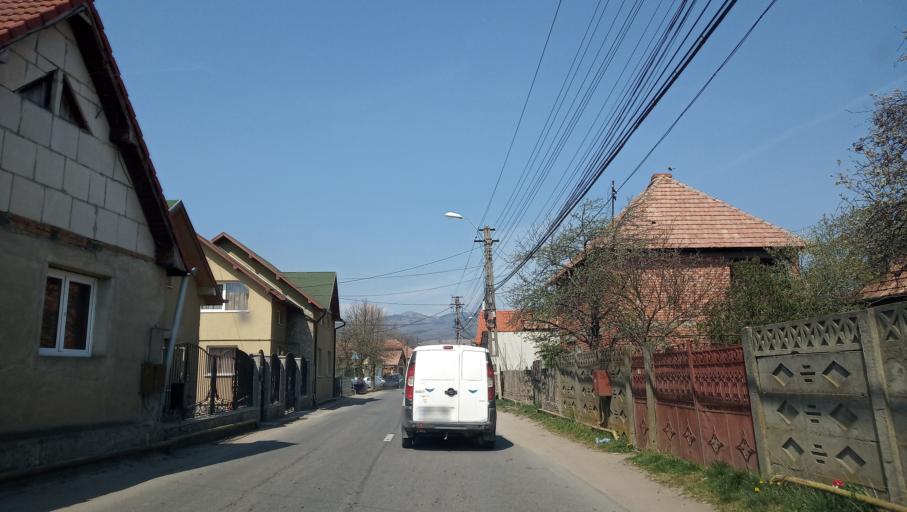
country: RO
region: Alba
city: Vurpar
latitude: 45.9905
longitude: 23.4843
